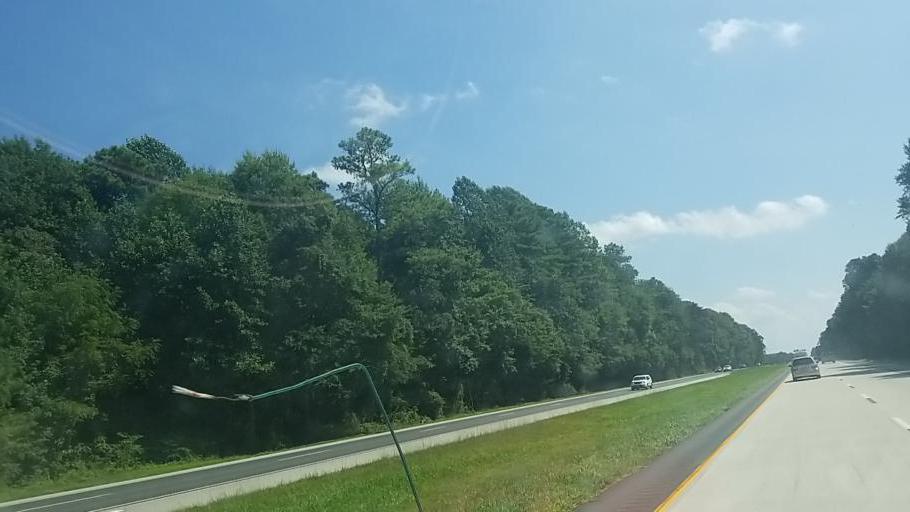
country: US
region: Delaware
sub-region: Sussex County
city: Milford
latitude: 38.8649
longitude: -75.4394
